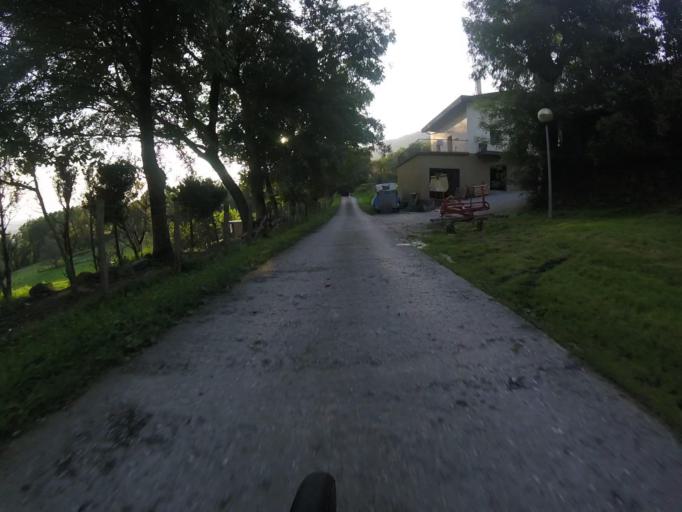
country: ES
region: Basque Country
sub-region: Provincia de Guipuzcoa
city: Lezo
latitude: 43.3347
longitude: -1.8565
